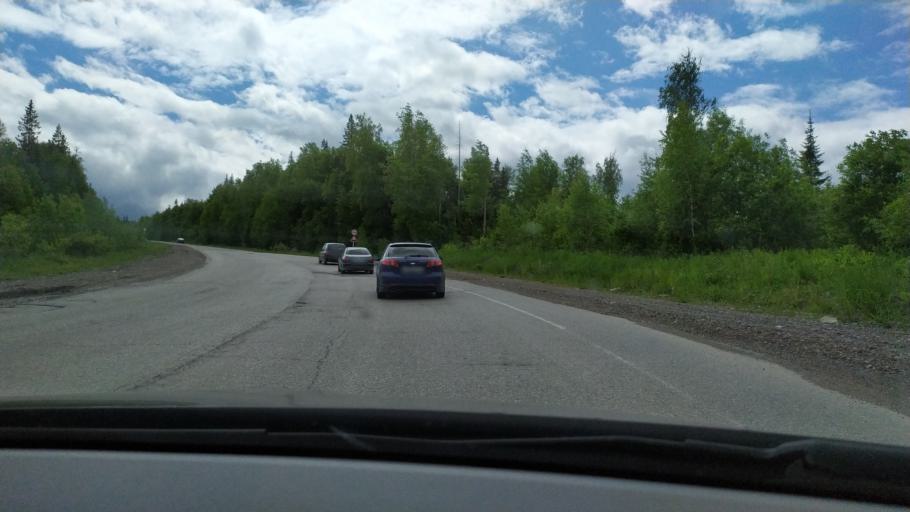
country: RU
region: Perm
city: Gremyachinsk
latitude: 58.4391
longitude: 57.8842
